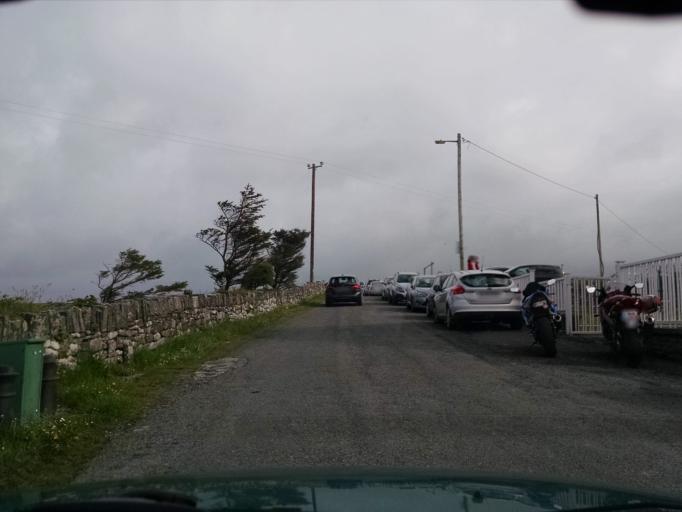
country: IE
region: Connaught
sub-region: County Galway
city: Bearna
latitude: 53.0257
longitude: -9.3674
